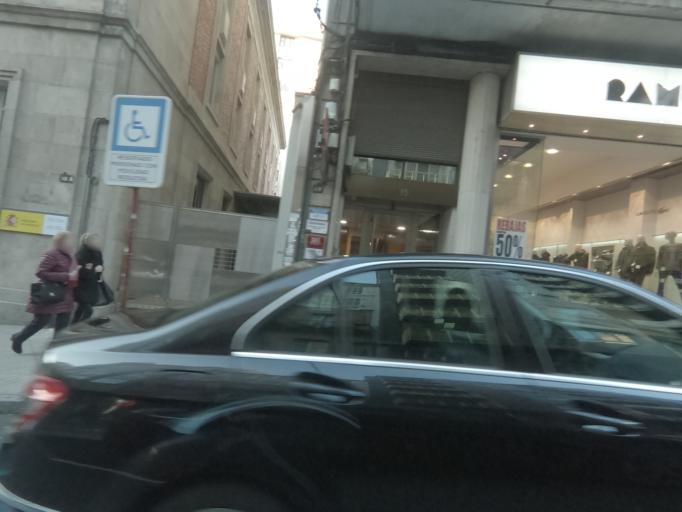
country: ES
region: Galicia
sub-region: Provincia de Ourense
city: Ourense
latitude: 42.3392
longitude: -7.8646
